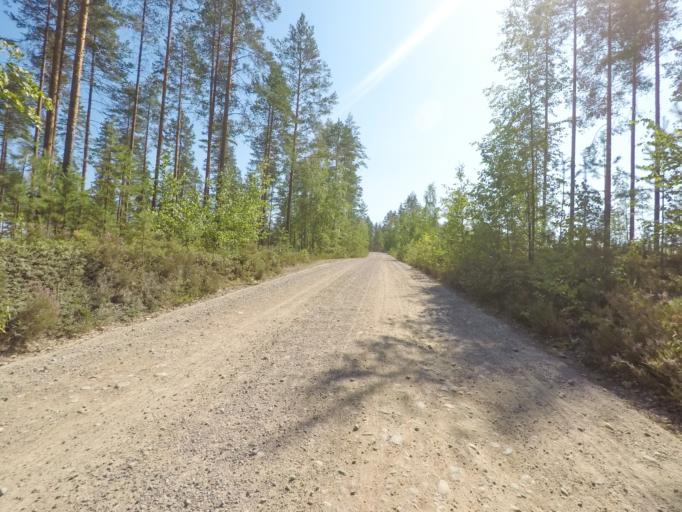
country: FI
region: Southern Savonia
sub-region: Mikkeli
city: Puumala
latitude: 61.4215
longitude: 28.0420
